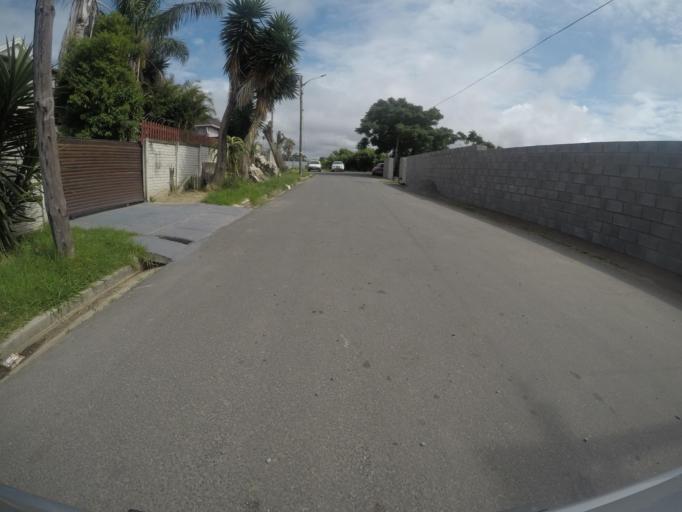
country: ZA
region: Eastern Cape
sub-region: Buffalo City Metropolitan Municipality
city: East London
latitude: -32.9977
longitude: 27.9093
